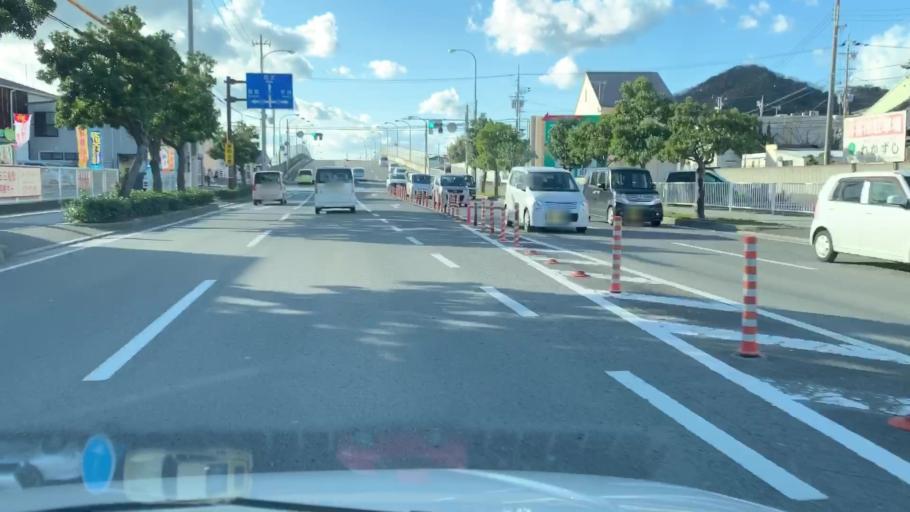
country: JP
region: Wakayama
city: Wakayama-shi
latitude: 34.2595
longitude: 135.1664
